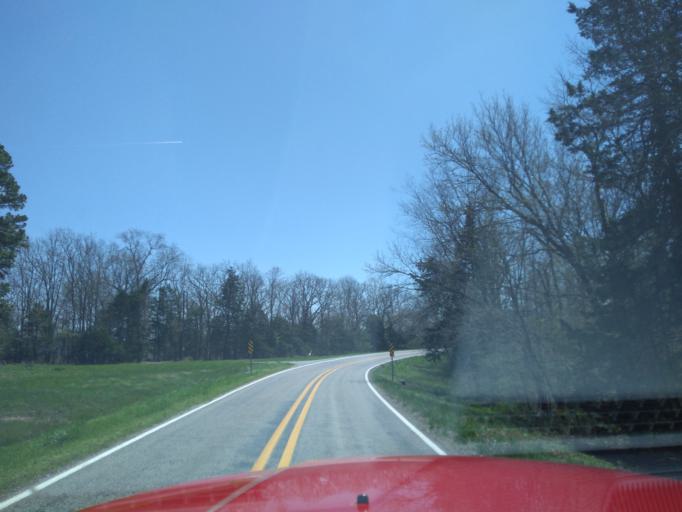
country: US
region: Arkansas
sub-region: Washington County
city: West Fork
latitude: 35.8080
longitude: -94.2564
